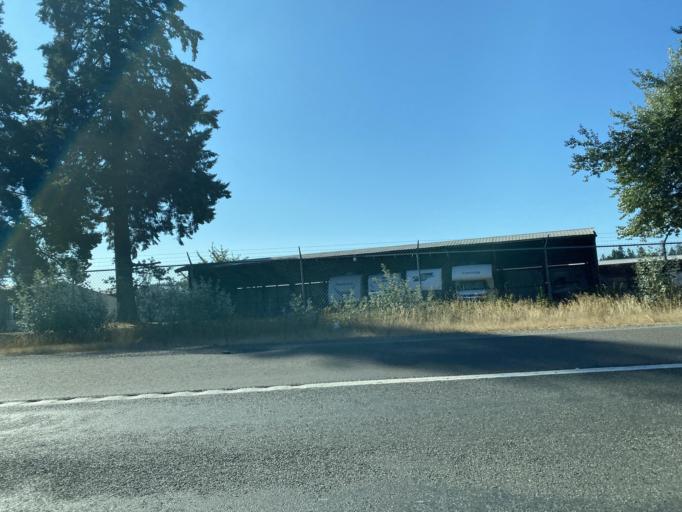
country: US
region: Washington
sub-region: Thurston County
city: Tanglewilde-Thompson Place
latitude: 46.9847
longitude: -122.7604
